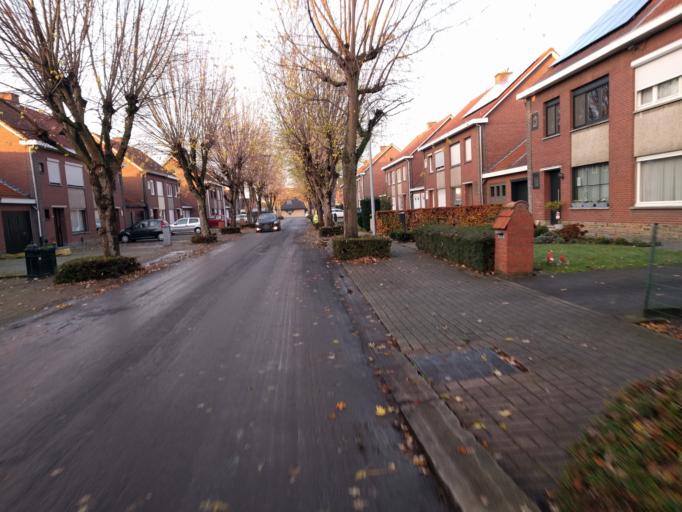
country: BE
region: Flanders
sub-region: Provincie West-Vlaanderen
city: Wevelgem
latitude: 50.8059
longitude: 3.1682
